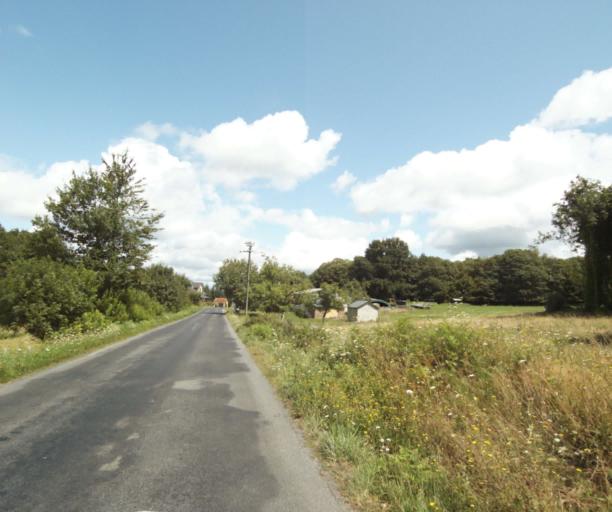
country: FR
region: Limousin
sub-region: Departement de la Correze
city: Sainte-Fortunade
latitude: 45.2012
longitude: 1.8268
